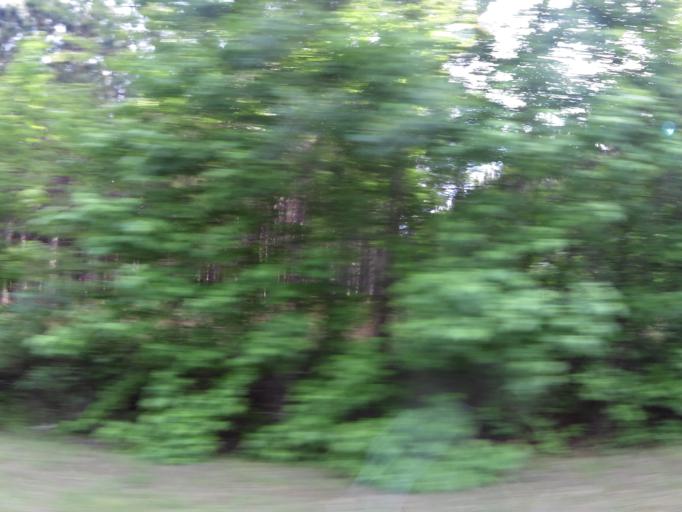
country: US
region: South Carolina
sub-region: Jasper County
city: Ridgeland
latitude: 32.5023
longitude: -81.1353
